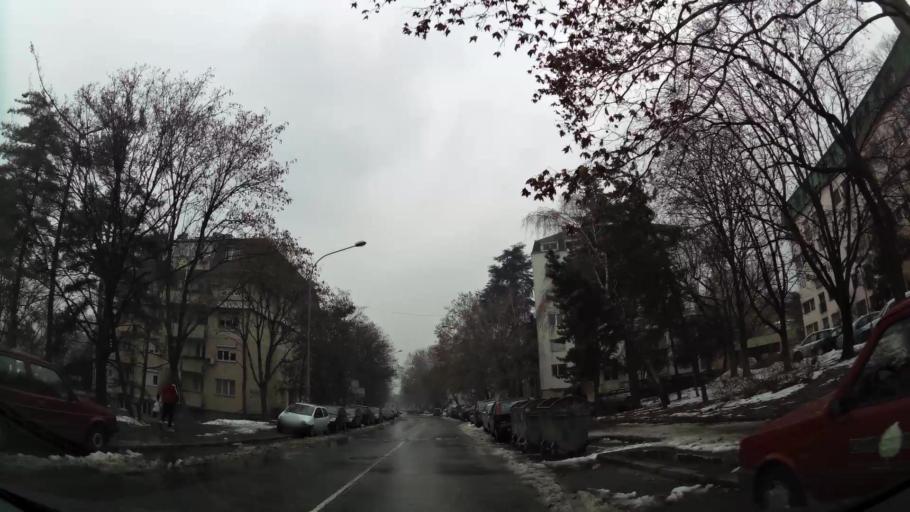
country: RS
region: Central Serbia
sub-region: Belgrade
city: Vozdovac
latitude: 44.7743
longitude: 20.4863
